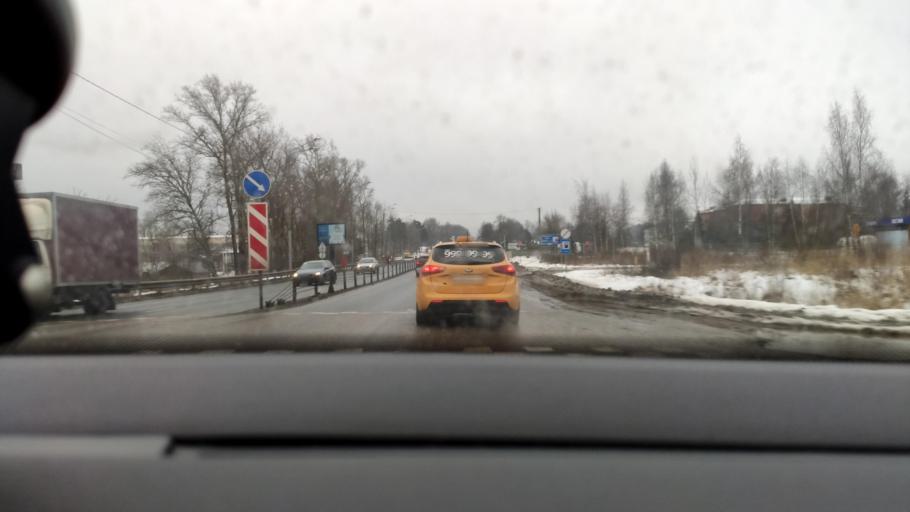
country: RU
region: Moskovskaya
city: Sergiyev Posad
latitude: 56.2825
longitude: 38.1243
